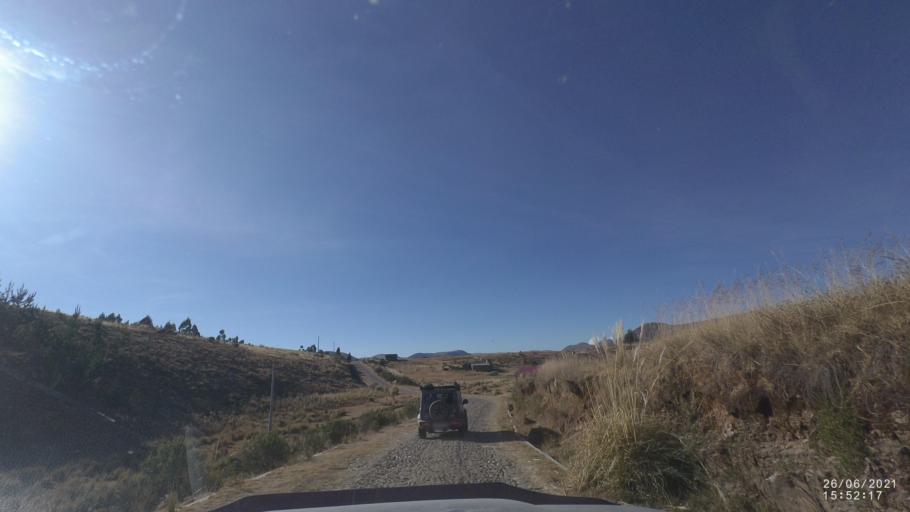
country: BO
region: Cochabamba
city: Arani
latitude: -17.8398
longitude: -65.7025
